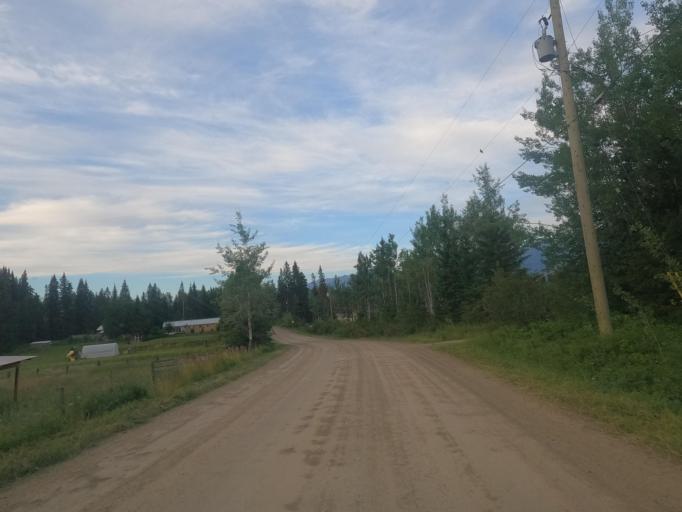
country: CA
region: British Columbia
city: Golden
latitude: 51.4407
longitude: -117.0412
